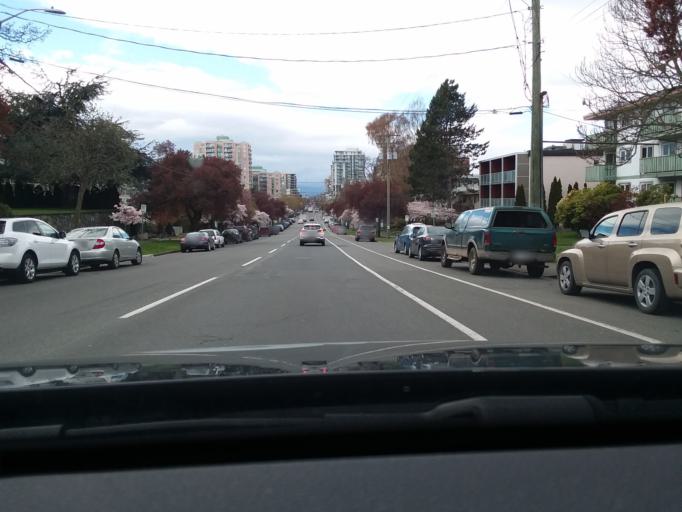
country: CA
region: British Columbia
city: Victoria
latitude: 48.4248
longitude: -123.3503
